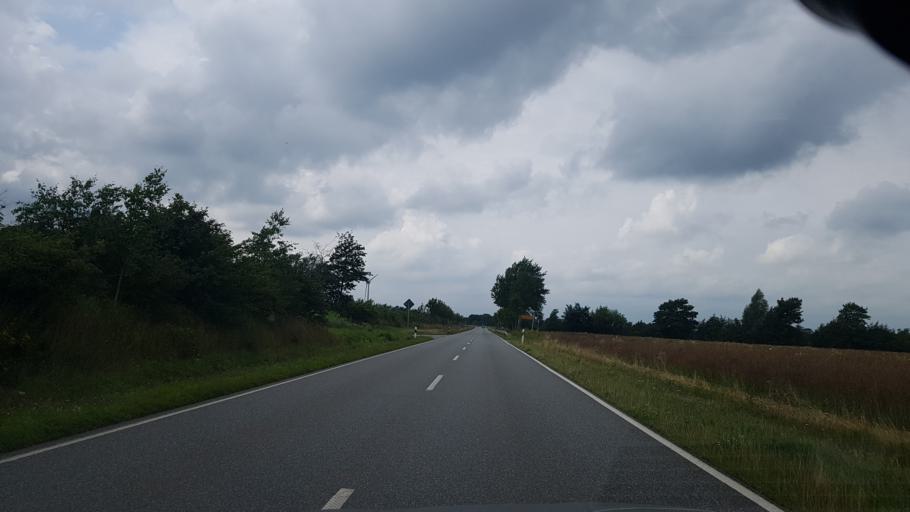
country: DE
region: Schleswig-Holstein
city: Boxlund
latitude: 54.8582
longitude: 9.1607
